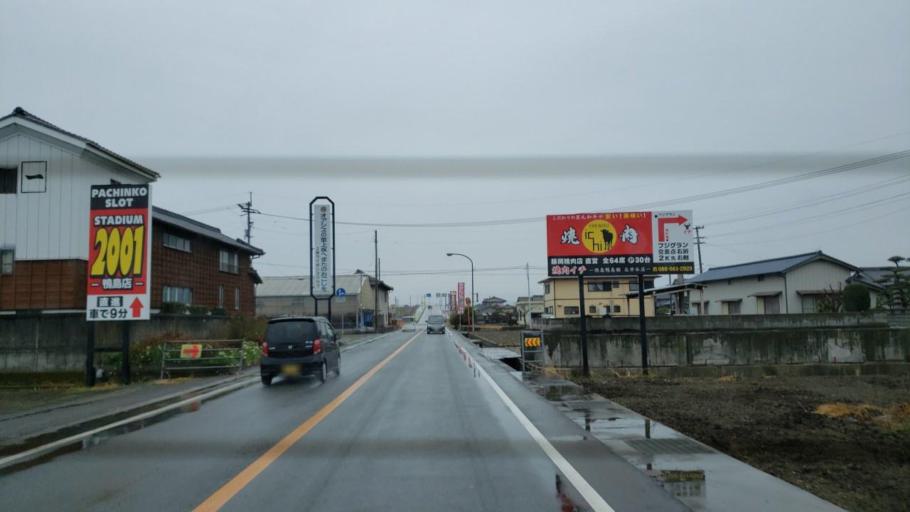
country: JP
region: Tokushima
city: Ishii
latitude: 34.1119
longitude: 134.4364
